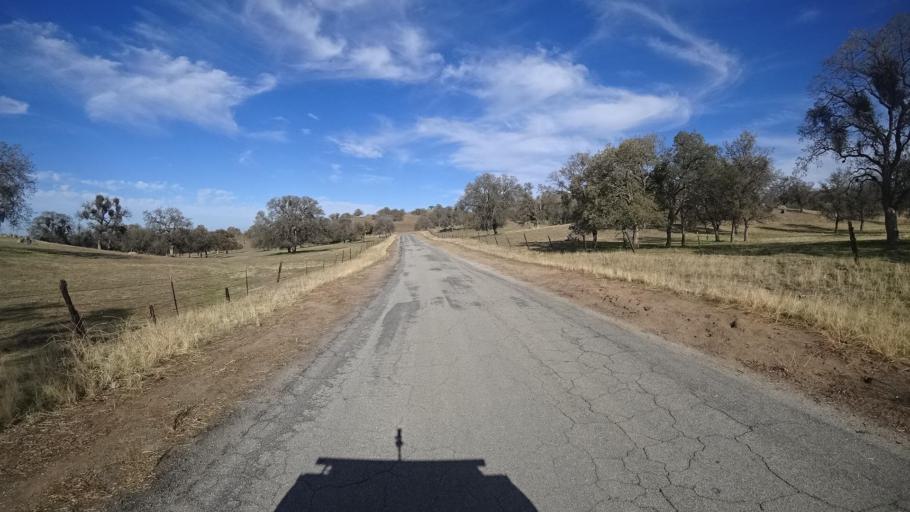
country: US
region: California
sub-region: Kern County
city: Oildale
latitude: 35.5836
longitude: -118.8233
